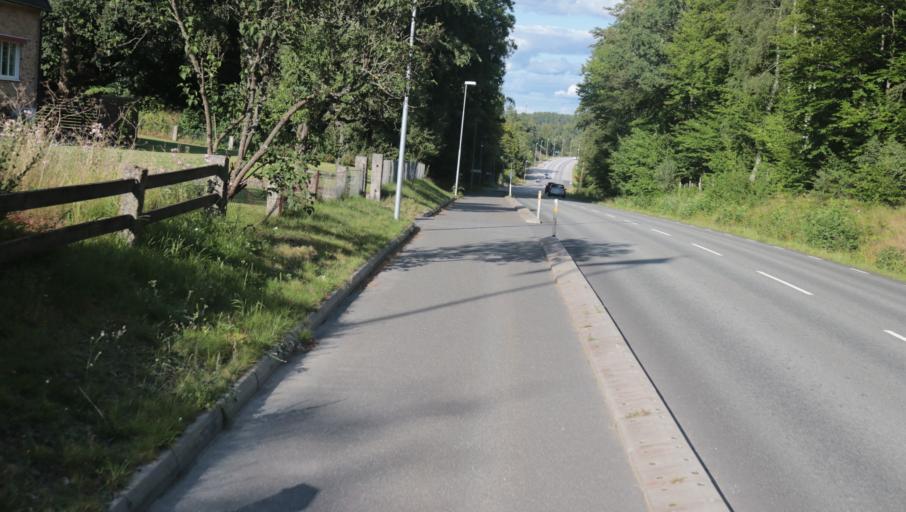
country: SE
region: Blekinge
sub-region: Karlshamns Kommun
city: Karlshamn
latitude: 56.1830
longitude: 14.9163
